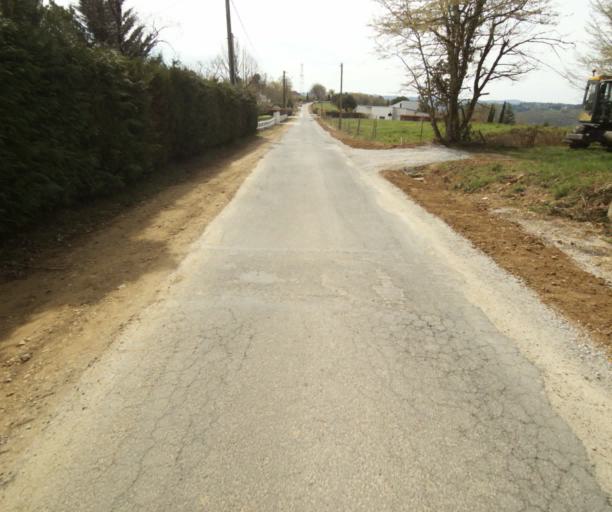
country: FR
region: Limousin
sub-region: Departement de la Correze
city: Naves
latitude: 45.2997
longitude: 1.7802
